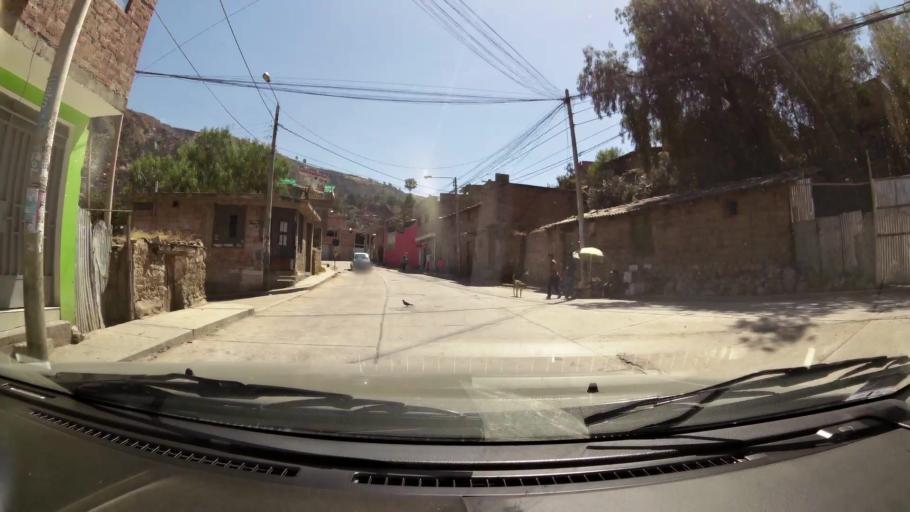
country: PE
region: Ayacucho
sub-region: Provincia de Huamanga
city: Ayacucho
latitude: -13.1633
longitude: -74.2364
